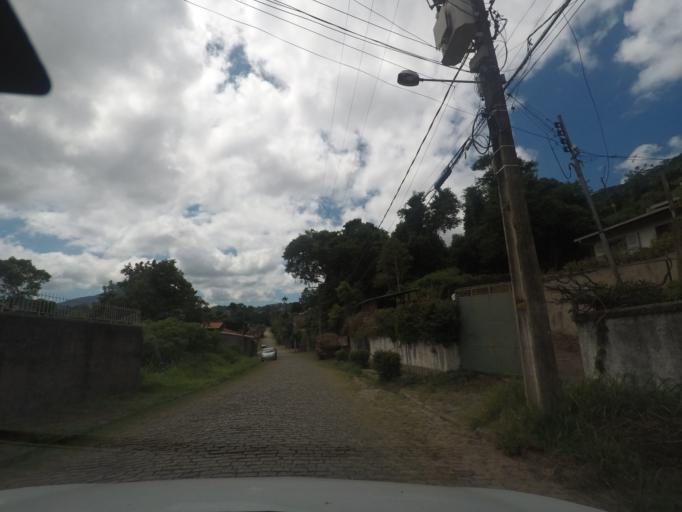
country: BR
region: Rio de Janeiro
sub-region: Teresopolis
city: Teresopolis
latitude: -22.3973
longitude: -42.9854
